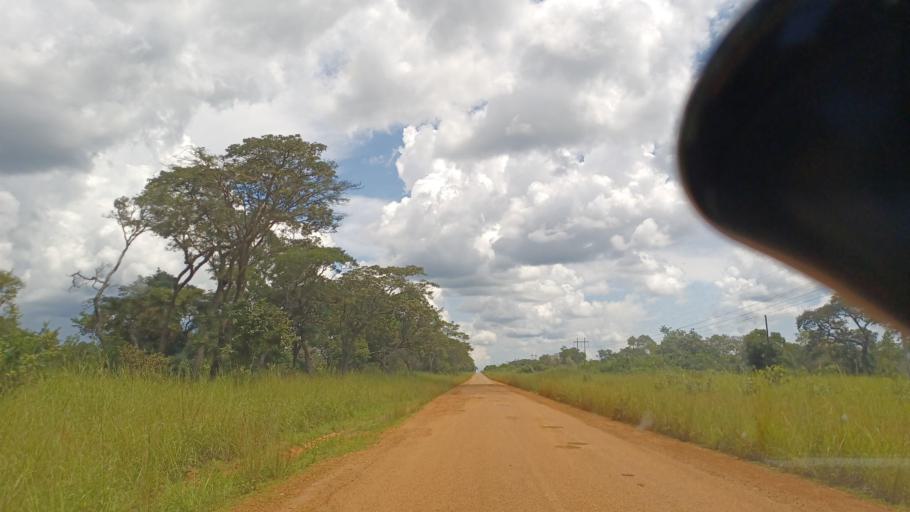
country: ZM
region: North-Western
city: Solwezi
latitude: -12.6985
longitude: 26.0379
